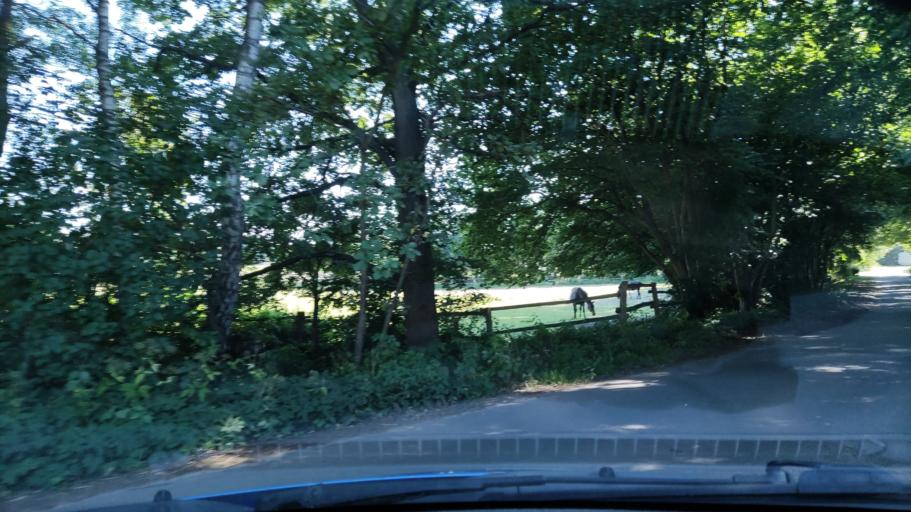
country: DE
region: Lower Saxony
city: Dahlenburg
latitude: 53.1770
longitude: 10.6928
